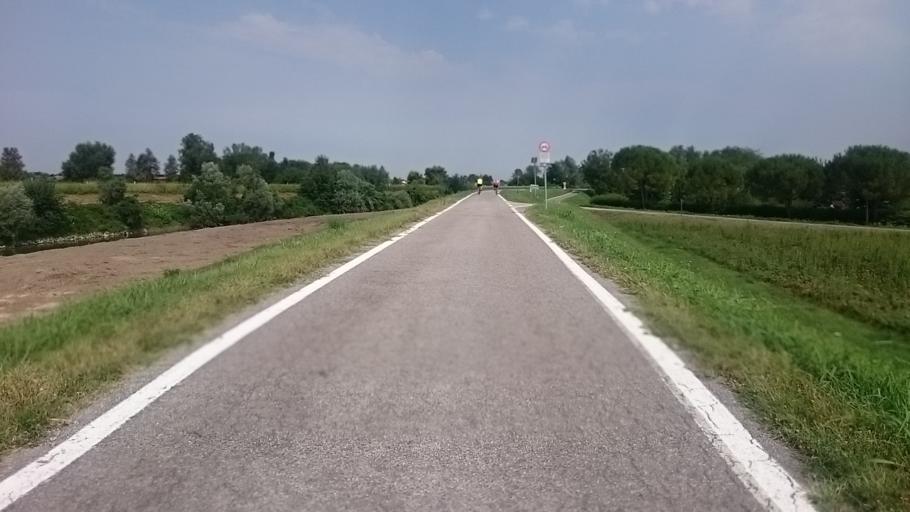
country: IT
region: Veneto
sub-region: Provincia di Padova
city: Casalserugo
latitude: 45.2976
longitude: 11.9292
